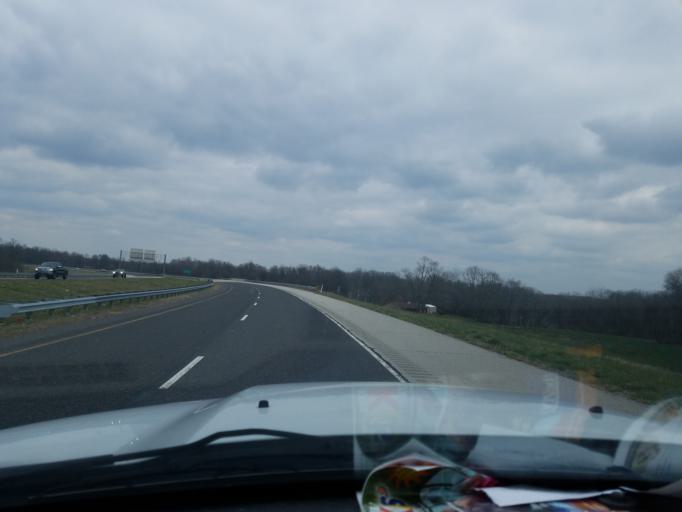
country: US
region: Indiana
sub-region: Vigo County
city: Terre Haute
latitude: 39.3746
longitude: -87.3764
